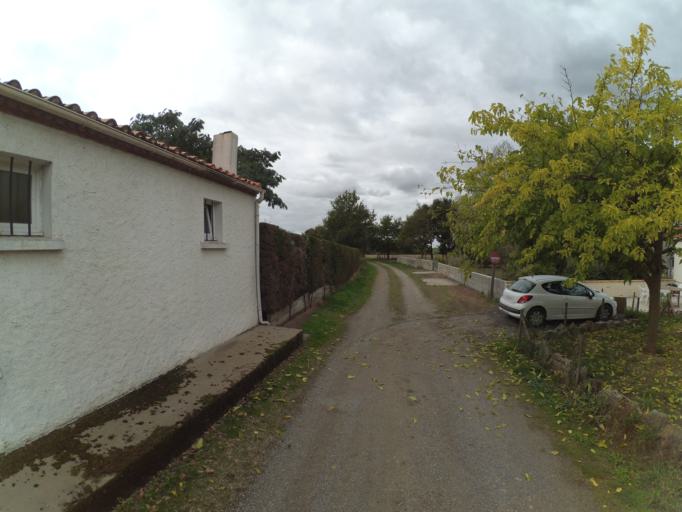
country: FR
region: Pays de la Loire
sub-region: Departement de la Loire-Atlantique
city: Remouille
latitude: 47.0486
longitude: -1.3450
